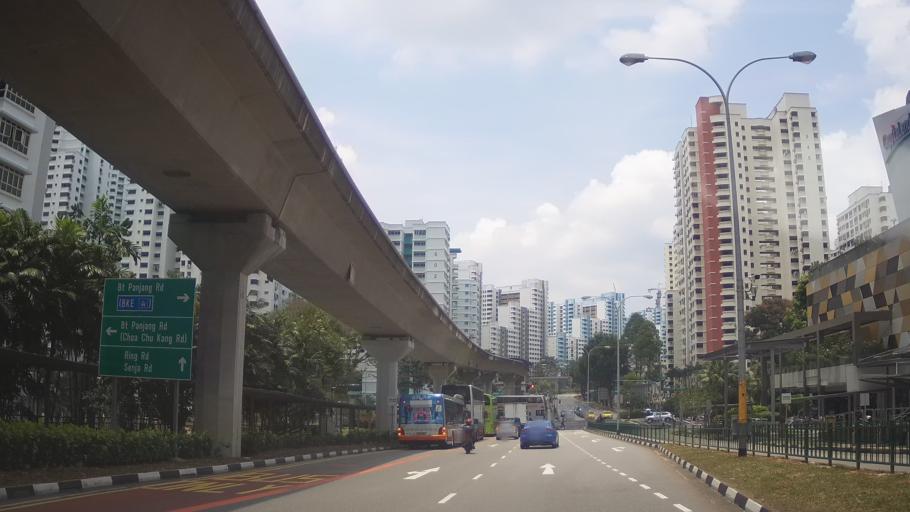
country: MY
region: Johor
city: Johor Bahru
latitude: 1.3797
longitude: 103.7640
